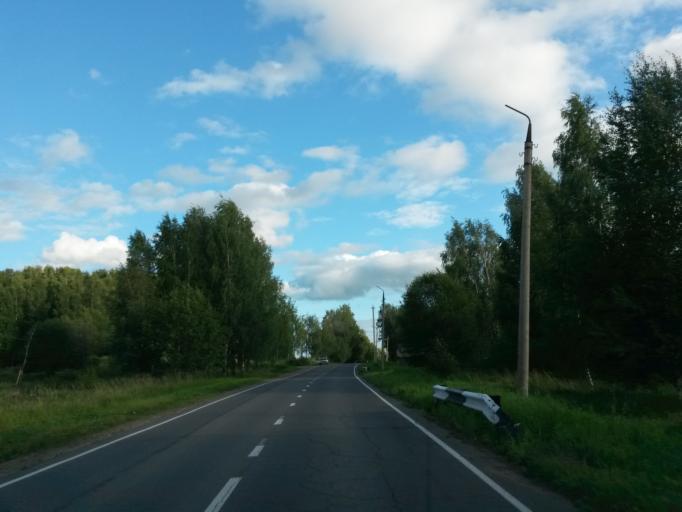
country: RU
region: Jaroslavl
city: Tutayev
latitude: 57.8985
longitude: 39.5264
